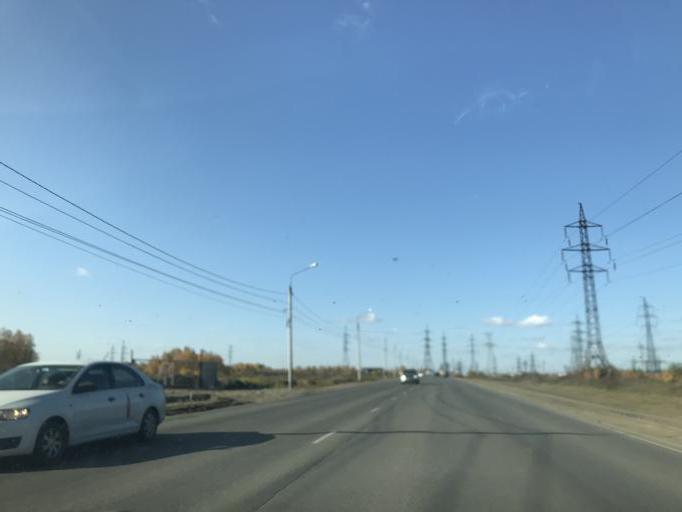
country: RU
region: Chelyabinsk
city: Roshchino
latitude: 55.2220
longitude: 61.2949
